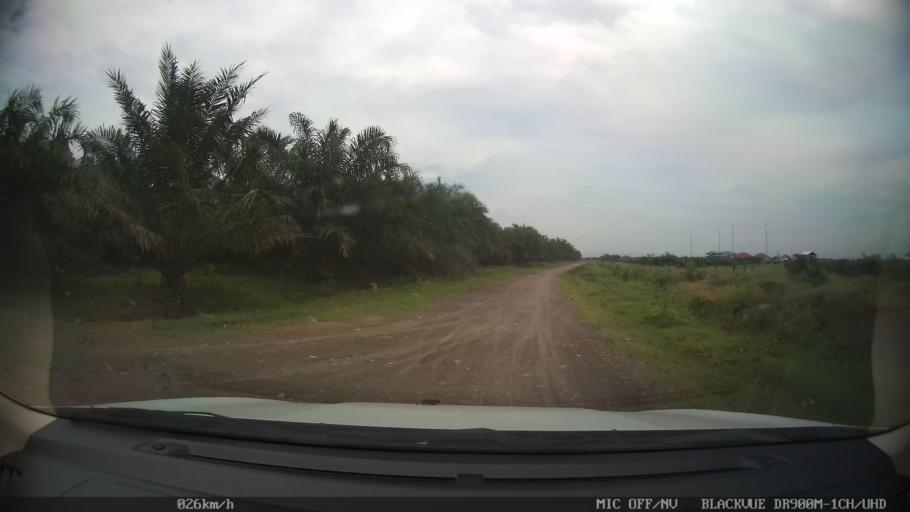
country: ID
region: North Sumatra
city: Sunggal
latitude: 3.6337
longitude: 98.5838
